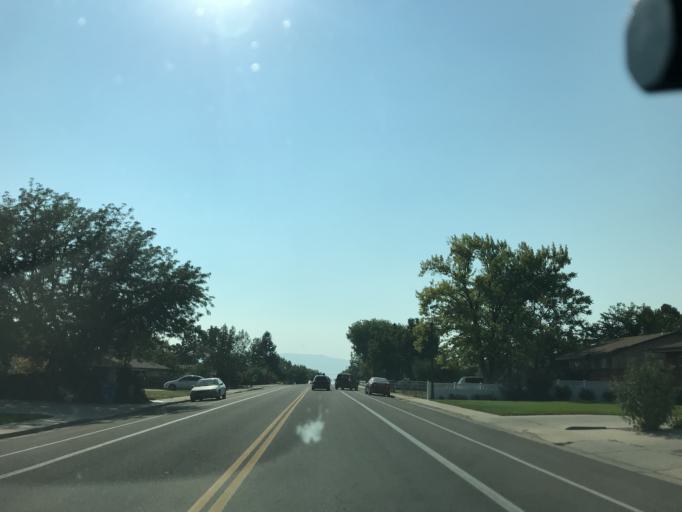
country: US
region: Utah
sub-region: Utah County
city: Orem
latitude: 40.2824
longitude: -111.6991
